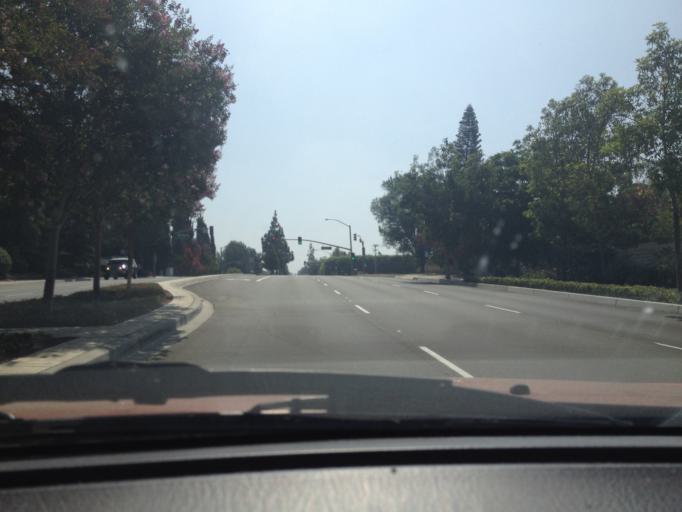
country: US
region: California
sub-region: Orange County
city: Yorba Linda
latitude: 33.8887
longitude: -117.8038
